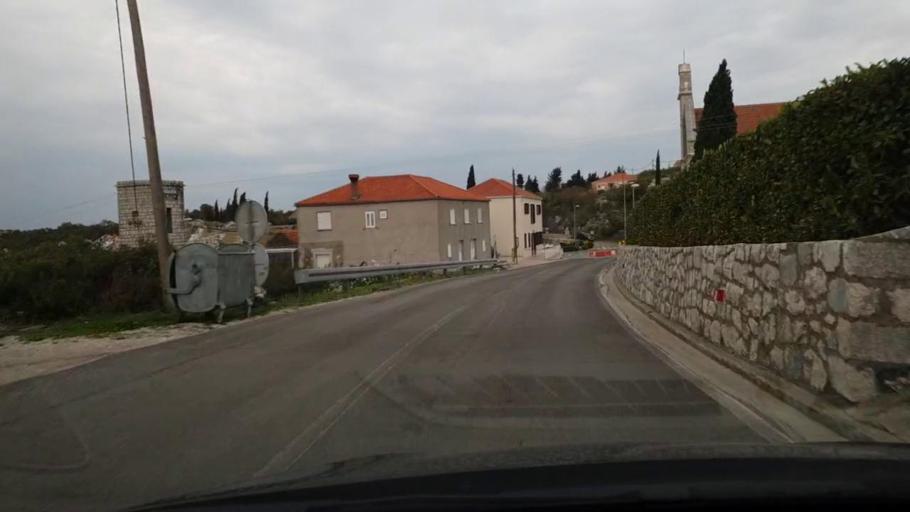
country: HR
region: Dubrovacko-Neretvanska
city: Cibaca
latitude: 42.6453
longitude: 18.1586
